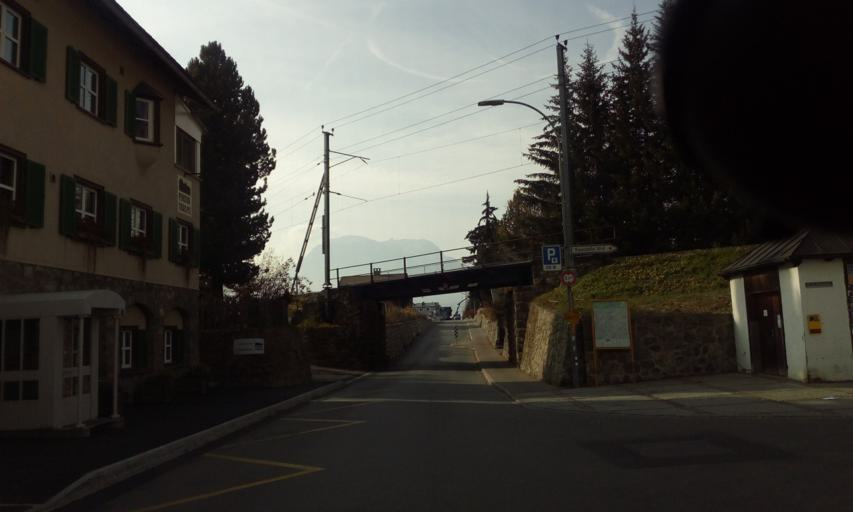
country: CH
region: Grisons
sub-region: Maloja District
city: Samedan
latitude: 46.5517
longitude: 9.8890
